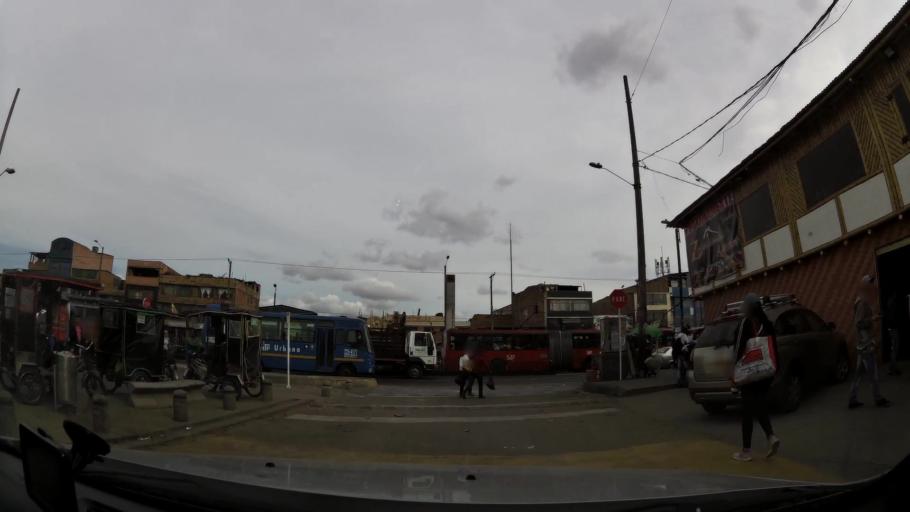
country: CO
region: Cundinamarca
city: Soacha
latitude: 4.6323
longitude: -74.1661
